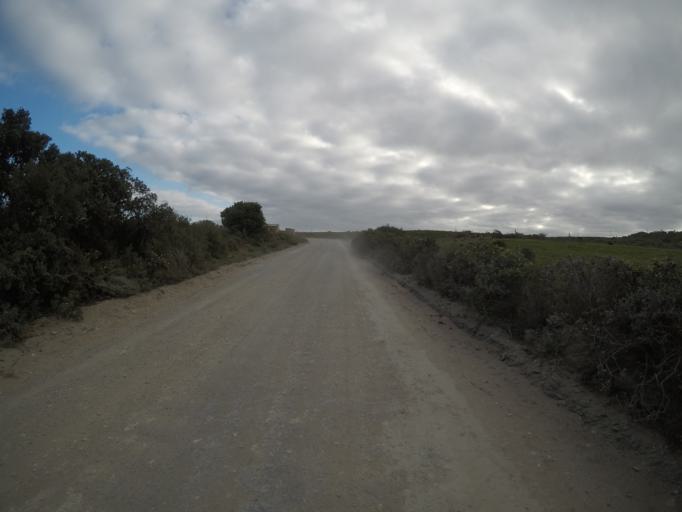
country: ZA
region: Western Cape
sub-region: Eden District Municipality
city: Riversdale
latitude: -34.4196
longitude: 21.3368
